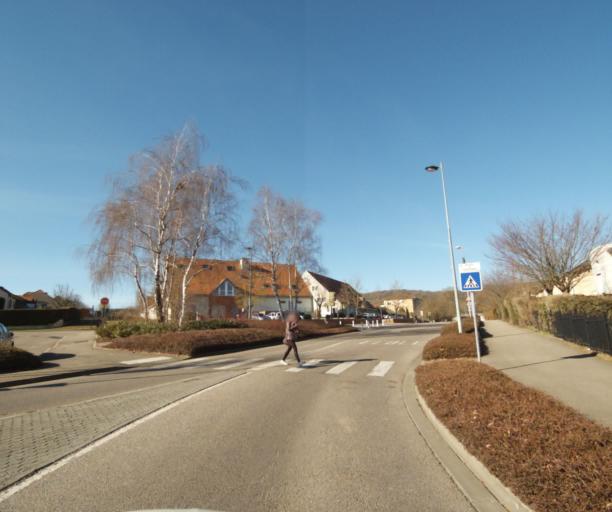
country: FR
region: Lorraine
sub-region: Departement de Meurthe-et-Moselle
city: Ludres
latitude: 48.6198
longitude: 6.1706
